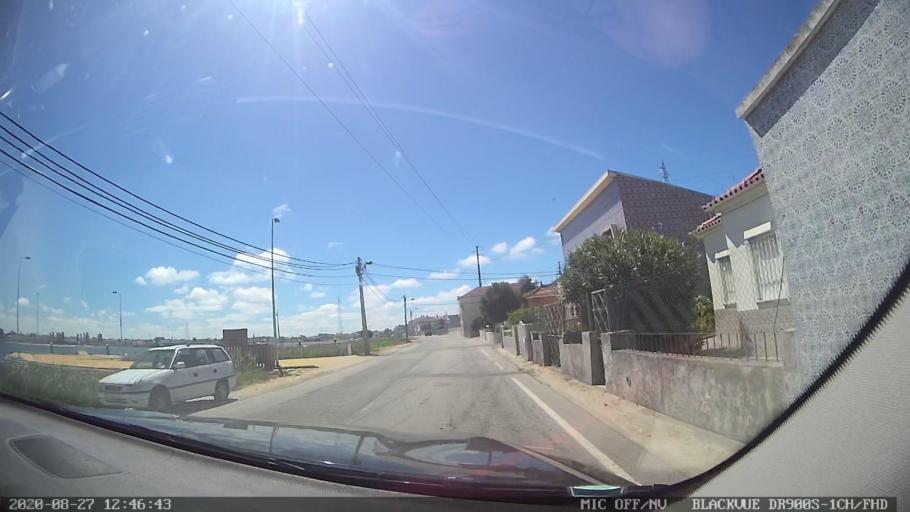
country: PT
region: Aveiro
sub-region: Ilhavo
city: Ilhavo
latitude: 40.6106
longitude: -8.6845
